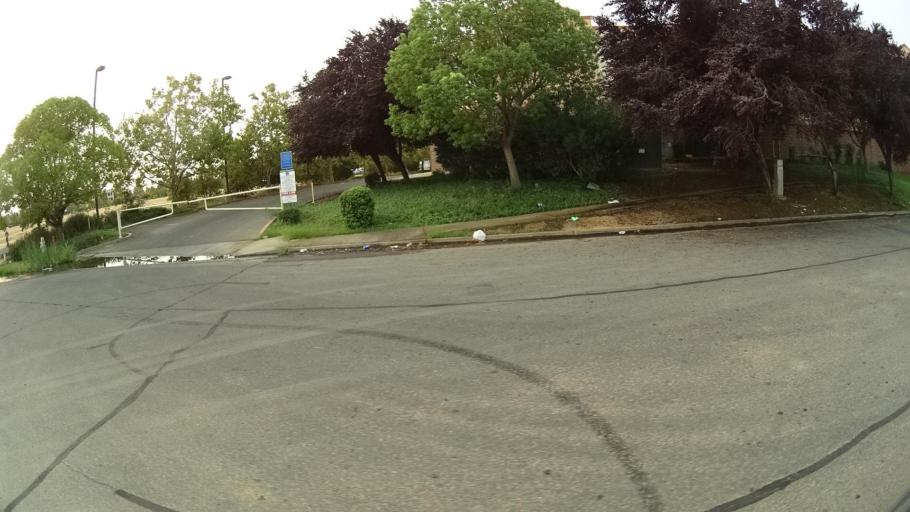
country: US
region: California
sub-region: Sacramento County
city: Laguna
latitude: 38.4192
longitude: -121.4043
